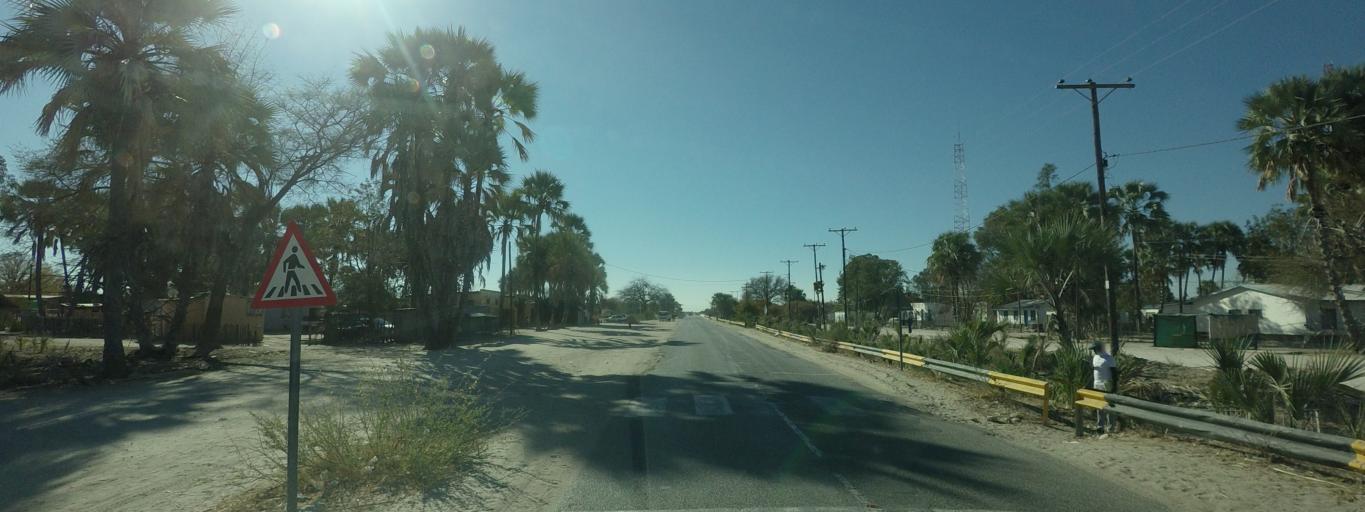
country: BW
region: Central
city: Nata
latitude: -20.2128
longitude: 26.1842
